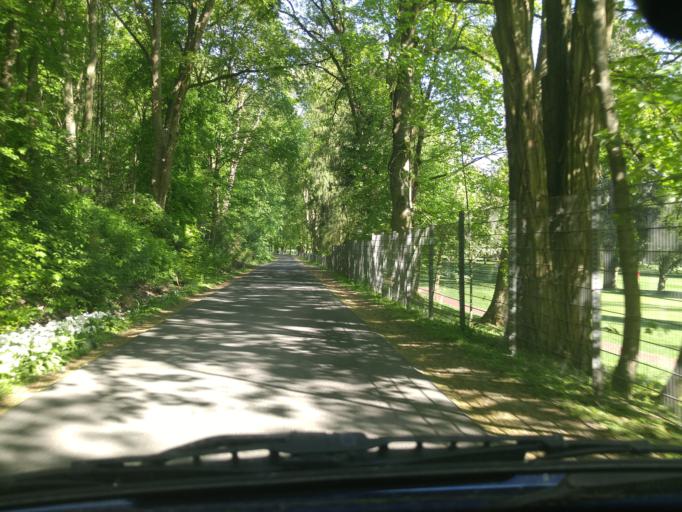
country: DE
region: Hesse
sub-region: Regierungsbezirk Darmstadt
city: Bad Nauheim
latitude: 50.3730
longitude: 8.7356
